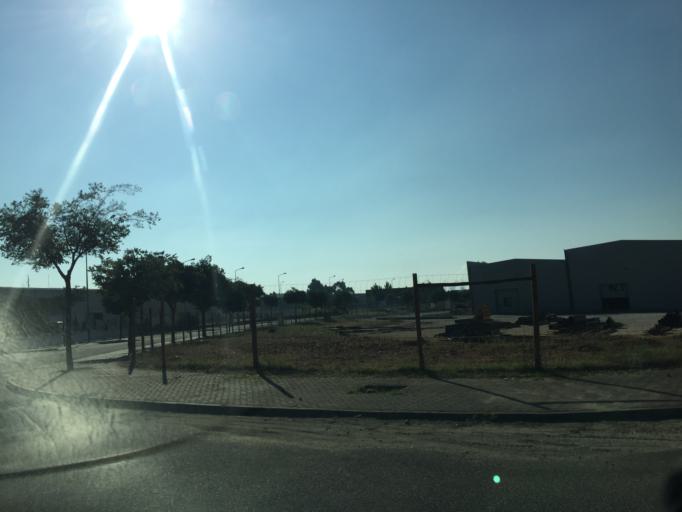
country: PT
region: Santarem
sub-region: Abrantes
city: Alferrarede
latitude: 39.4923
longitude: -8.1882
